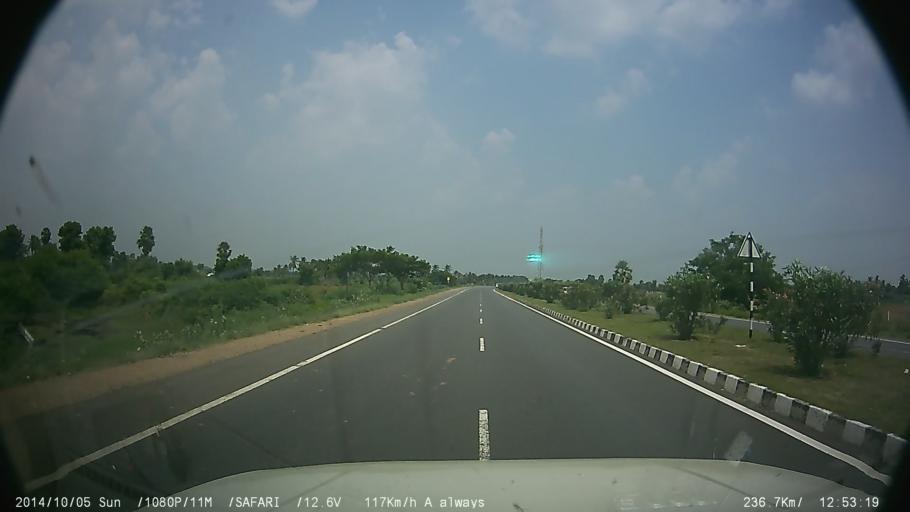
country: IN
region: Tamil Nadu
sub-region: Cuddalore
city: Panruti
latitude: 11.7458
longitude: 79.3670
